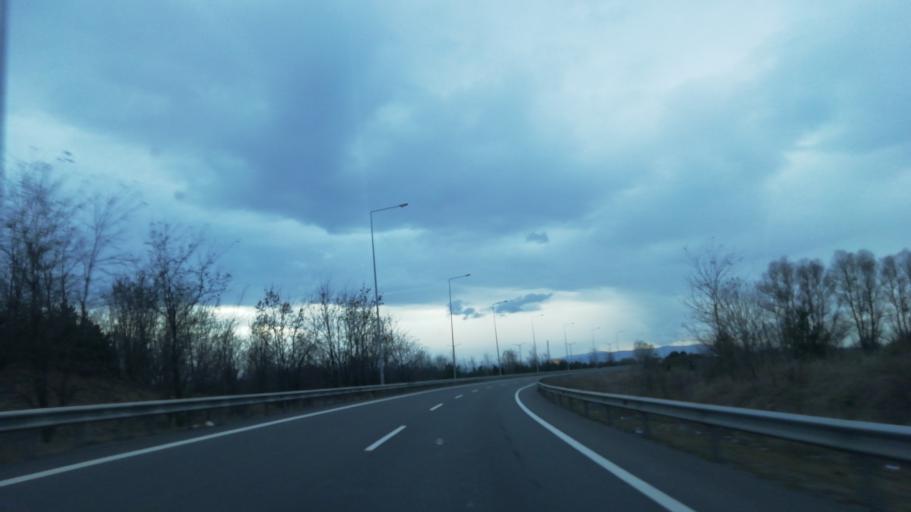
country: TR
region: Bolu
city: Gerede
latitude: 40.7397
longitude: 32.1927
